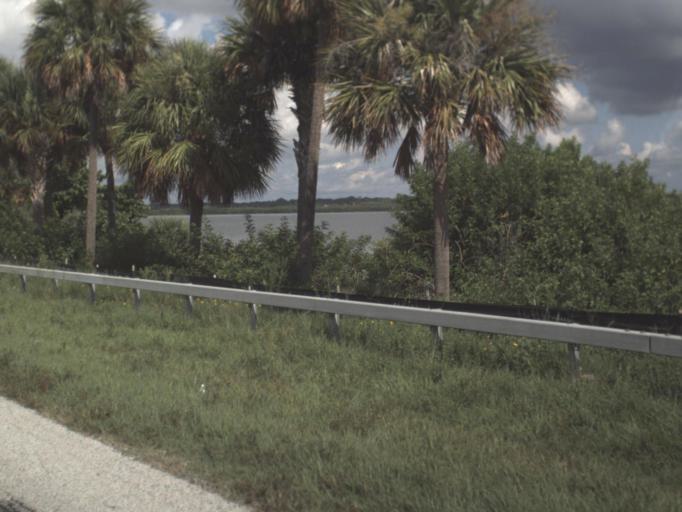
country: US
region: Florida
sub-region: Pinellas County
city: Safety Harbor
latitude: 27.9630
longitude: -82.6826
